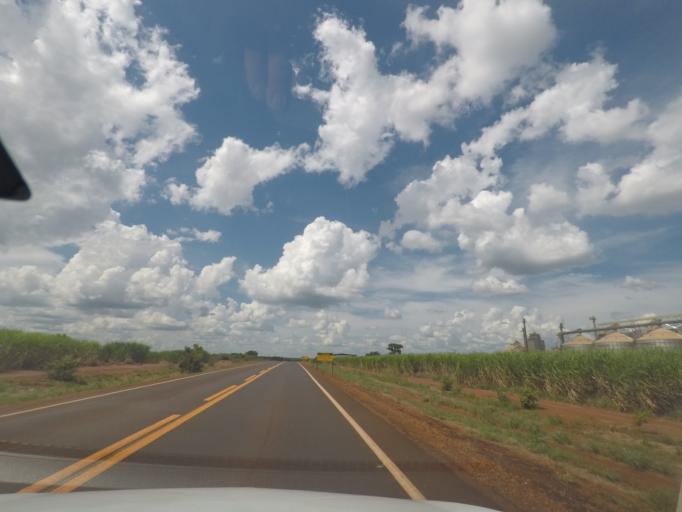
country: BR
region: Minas Gerais
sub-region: Conceicao Das Alagoas
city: Conceicao das Alagoas
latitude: -19.8080
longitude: -48.5820
